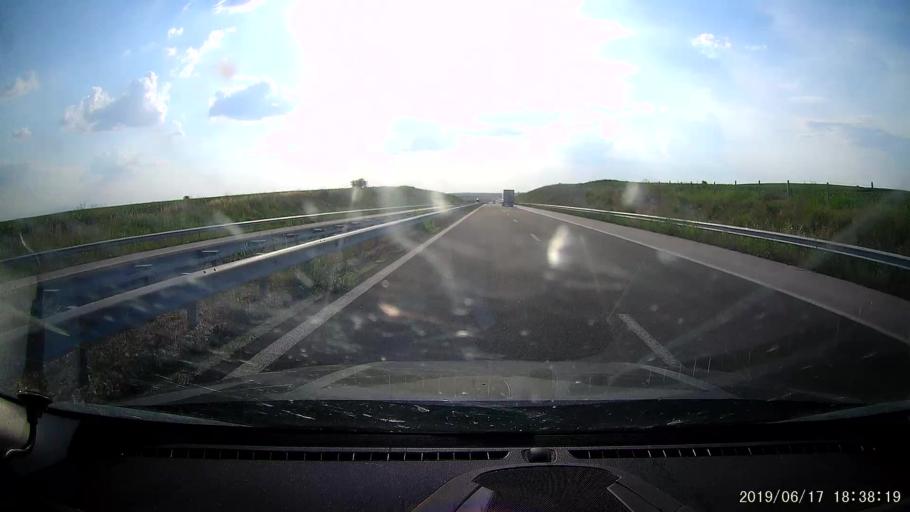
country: BG
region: Stara Zagora
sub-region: Obshtina Chirpan
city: Chirpan
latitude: 42.1362
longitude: 25.3404
